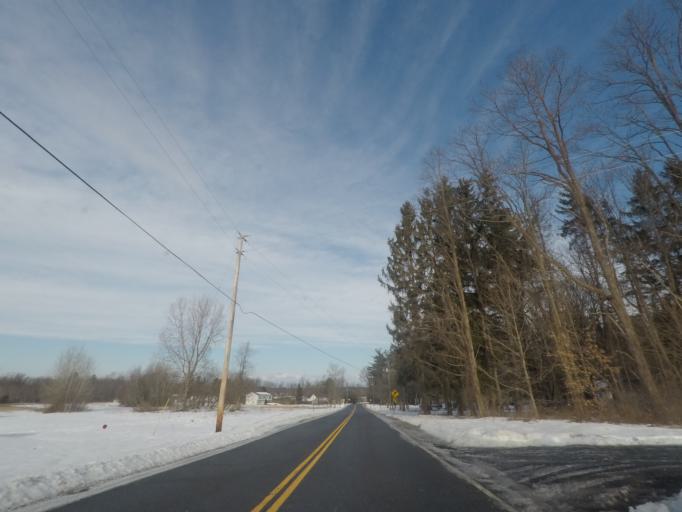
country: US
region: New York
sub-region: Saratoga County
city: Mechanicville
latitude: 42.8560
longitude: -73.7338
